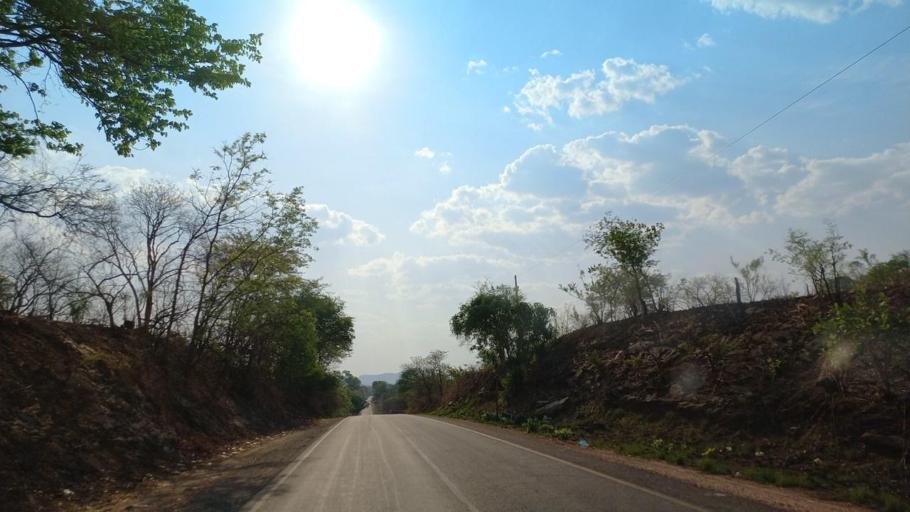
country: ZM
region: Lusaka
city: Luangwa
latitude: -14.9812
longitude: 30.1456
